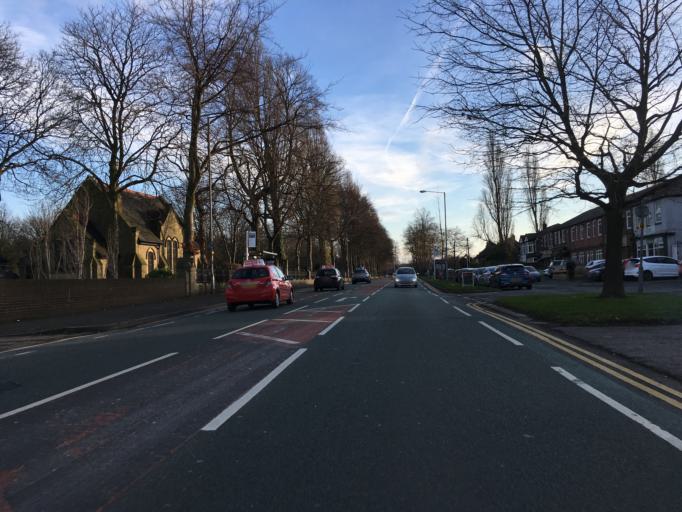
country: GB
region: England
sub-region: Manchester
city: Chorlton cum Hardy
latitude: 53.4304
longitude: -2.2669
